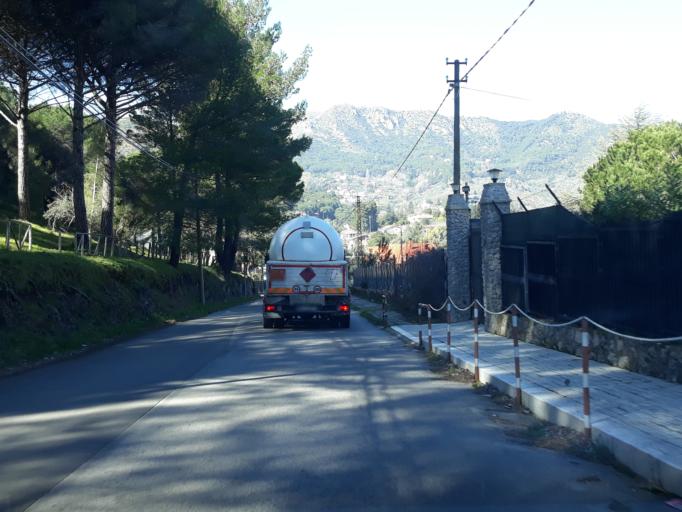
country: IT
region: Sicily
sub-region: Palermo
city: Piano dei Geli
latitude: 38.0851
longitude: 13.2668
